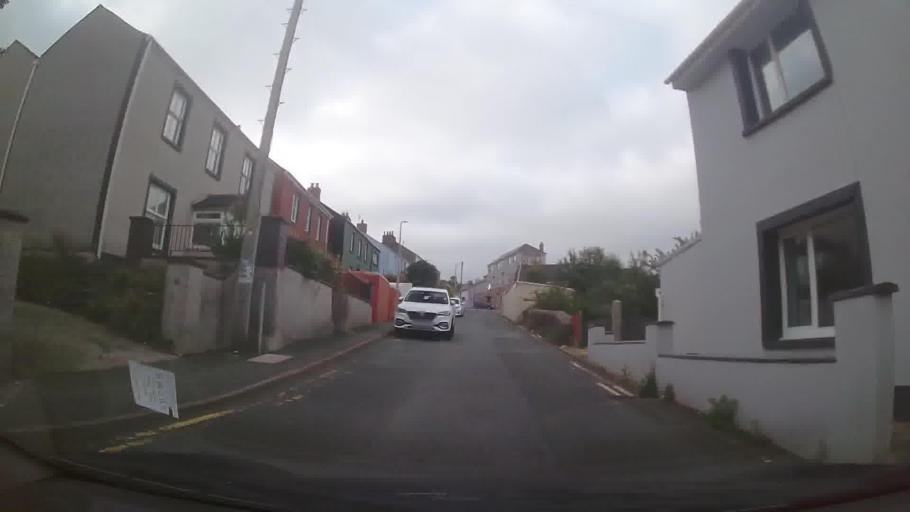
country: GB
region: Wales
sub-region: Pembrokeshire
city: Milford Haven
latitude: 51.7116
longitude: -5.0438
